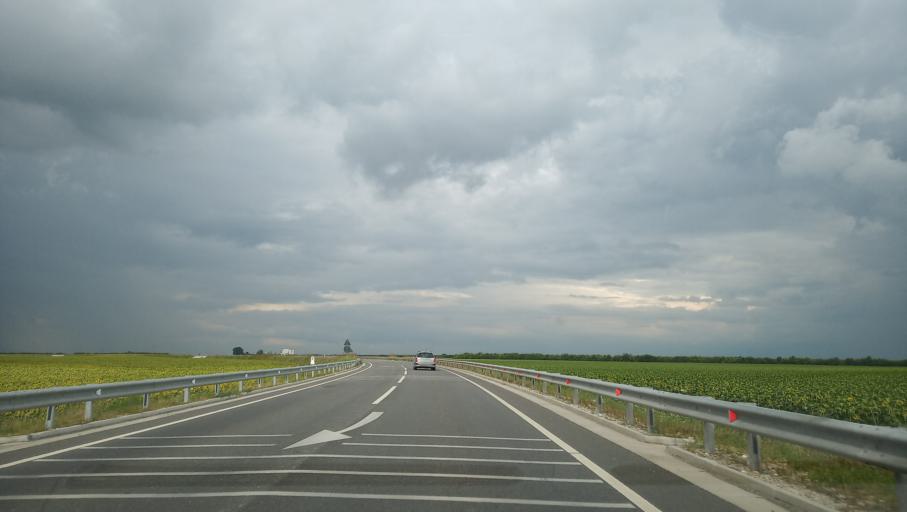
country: RO
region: Olt
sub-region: Comuna Deveselu
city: Comanca
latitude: 44.0950
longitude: 24.3787
